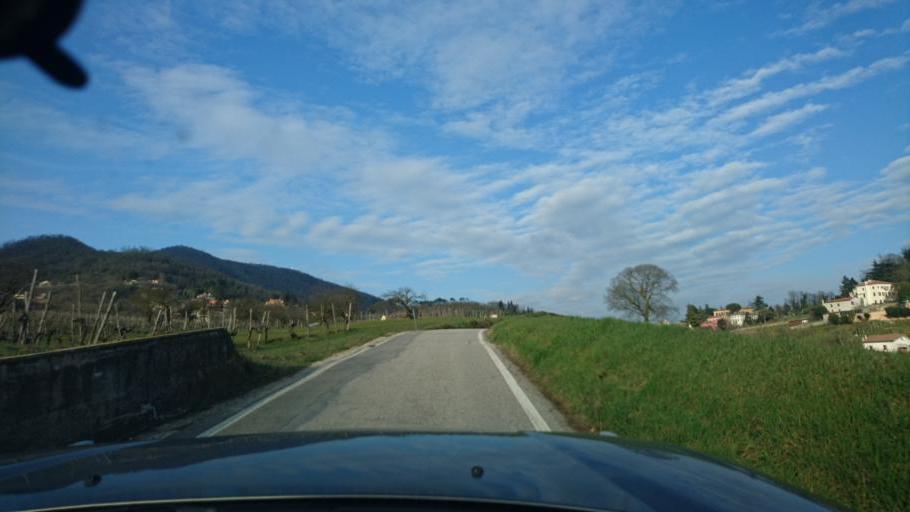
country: IT
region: Veneto
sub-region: Provincia di Padova
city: Vo
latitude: 45.3448
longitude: 11.6669
